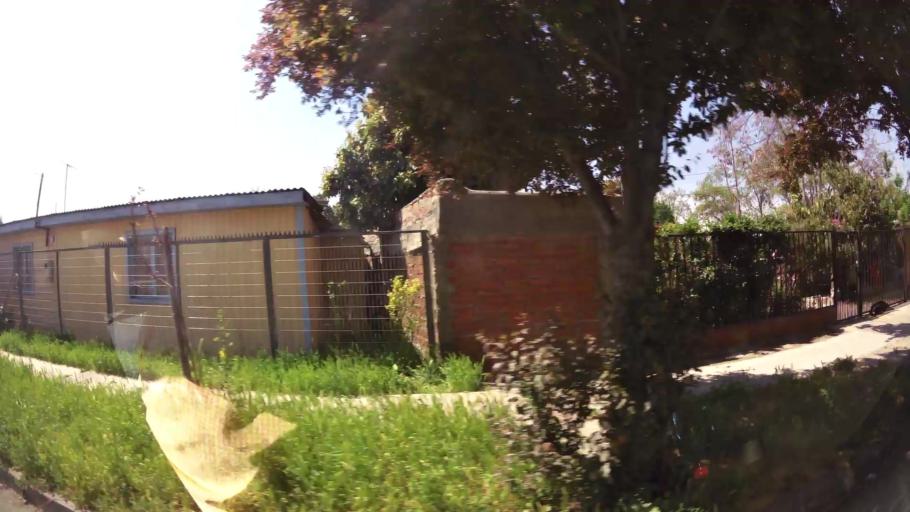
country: CL
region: Santiago Metropolitan
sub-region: Provincia de Talagante
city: Talagante
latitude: -33.6510
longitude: -70.9255
